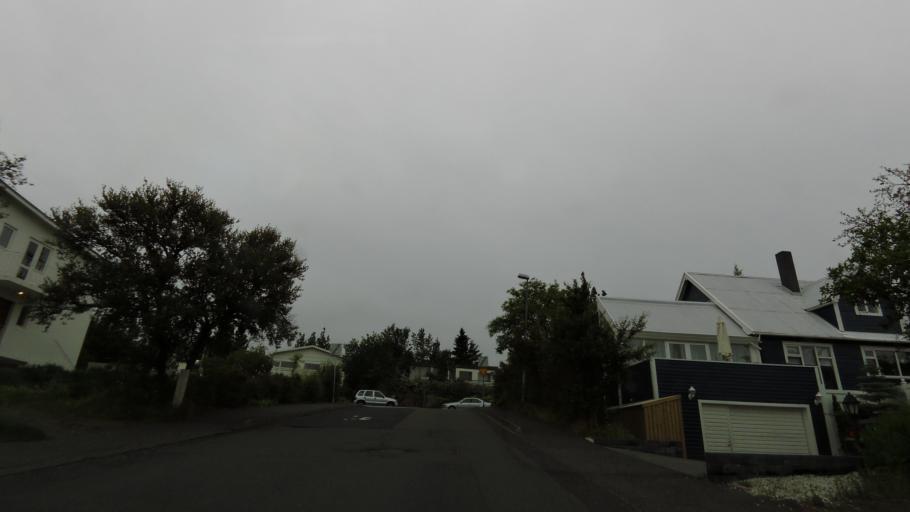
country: IS
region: Capital Region
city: Kopavogur
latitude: 64.1080
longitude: -21.8938
